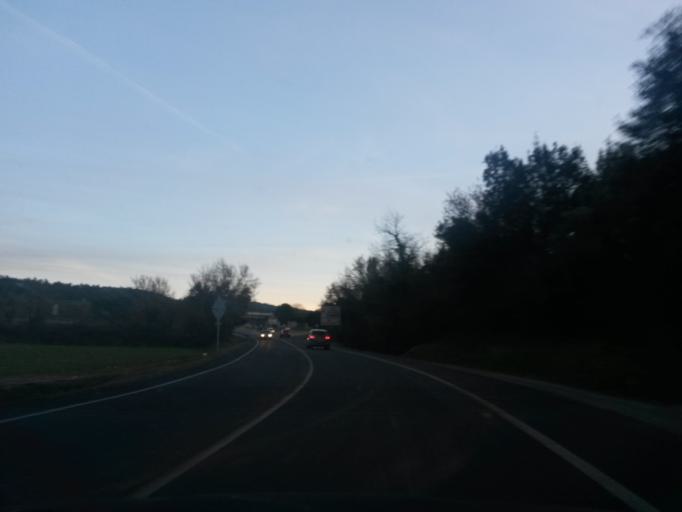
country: ES
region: Catalonia
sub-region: Provincia de Girona
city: Quart d'Onyar
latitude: 41.9627
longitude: 2.8449
